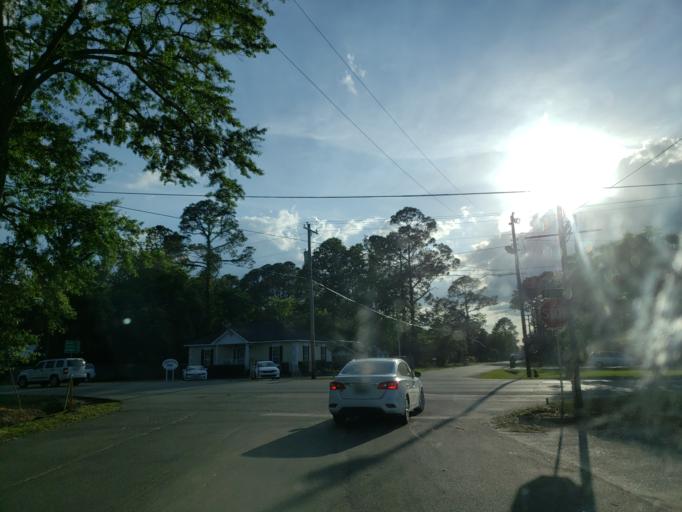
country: US
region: Georgia
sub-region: Cook County
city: Adel
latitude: 31.1331
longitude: -83.4331
